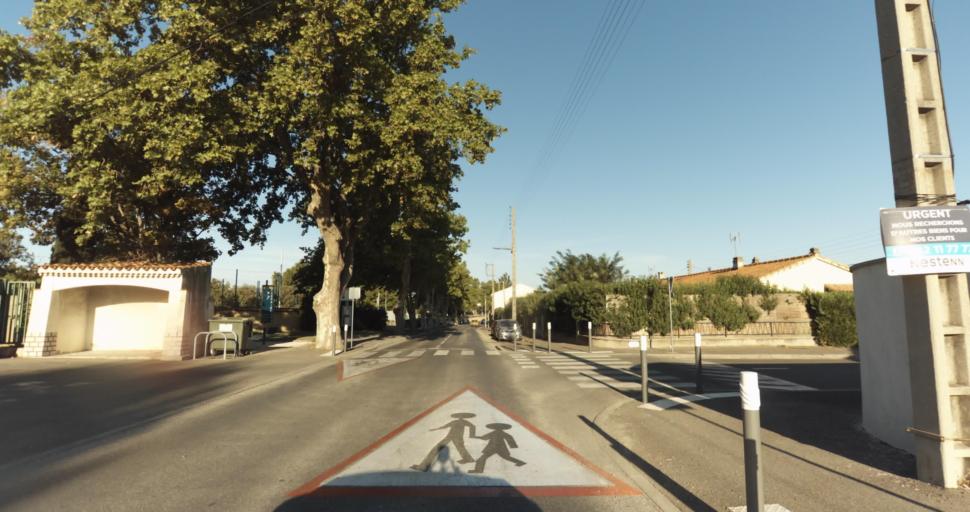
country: FR
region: Provence-Alpes-Cote d'Azur
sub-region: Departement des Bouches-du-Rhone
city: Miramas
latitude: 43.5787
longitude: 5.0058
